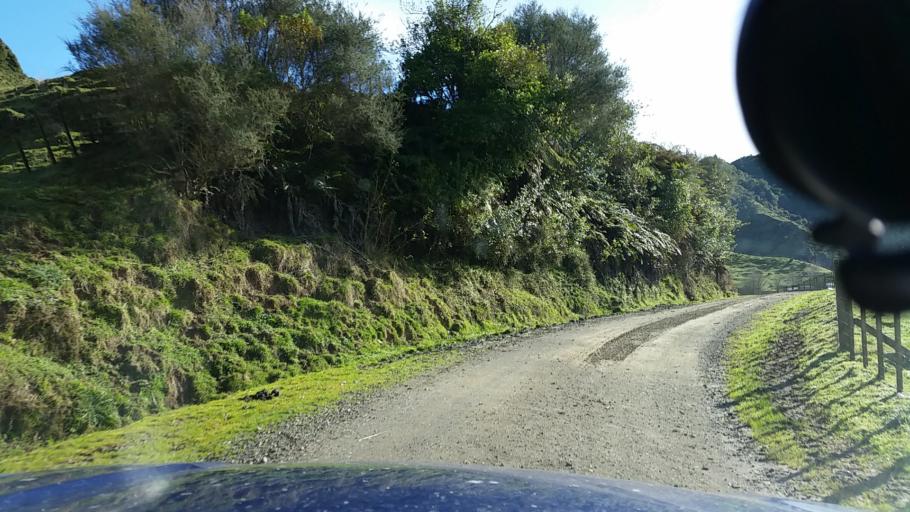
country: NZ
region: Taranaki
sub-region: New Plymouth District
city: Waitara
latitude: -39.0520
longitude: 174.7477
